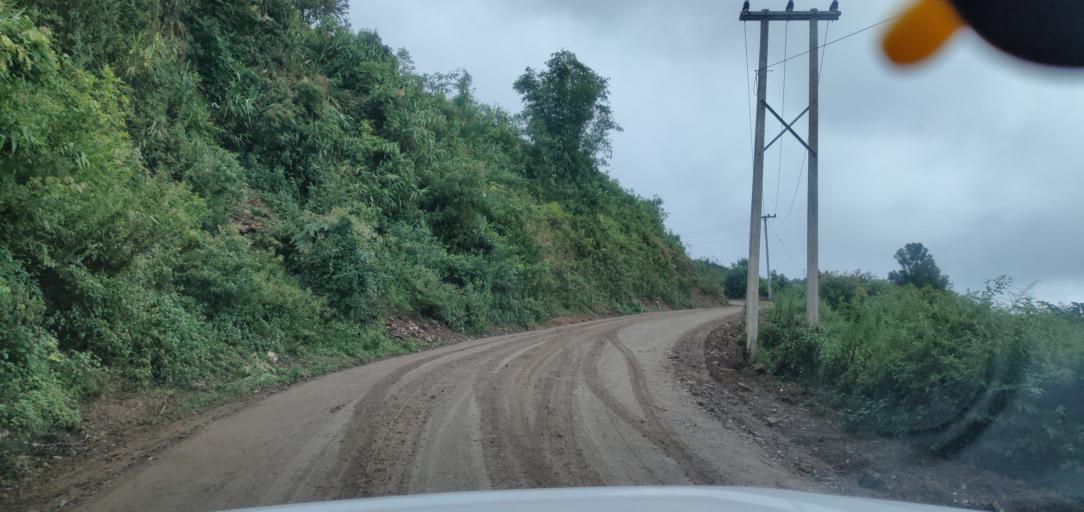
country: LA
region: Phongsali
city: Phongsali
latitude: 21.4269
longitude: 102.1697
